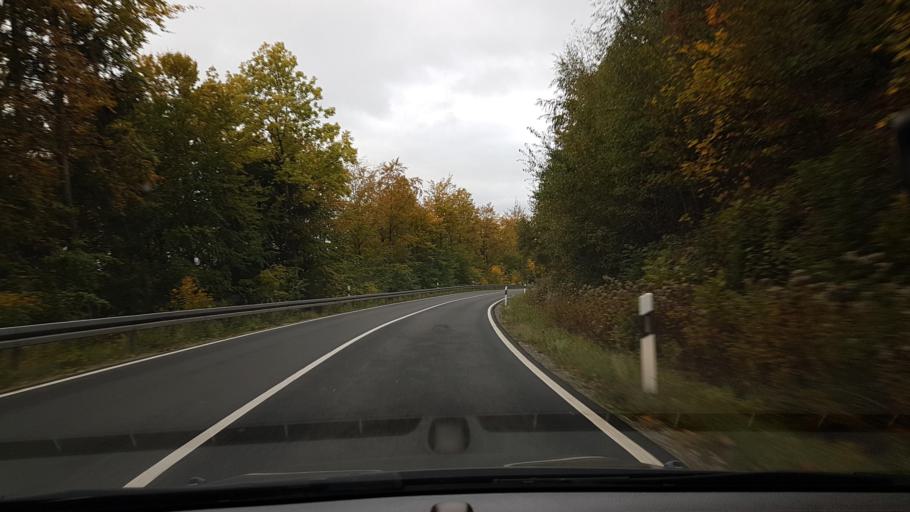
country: DE
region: Lower Saxony
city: Bad Grund
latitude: 51.8087
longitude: 10.2521
